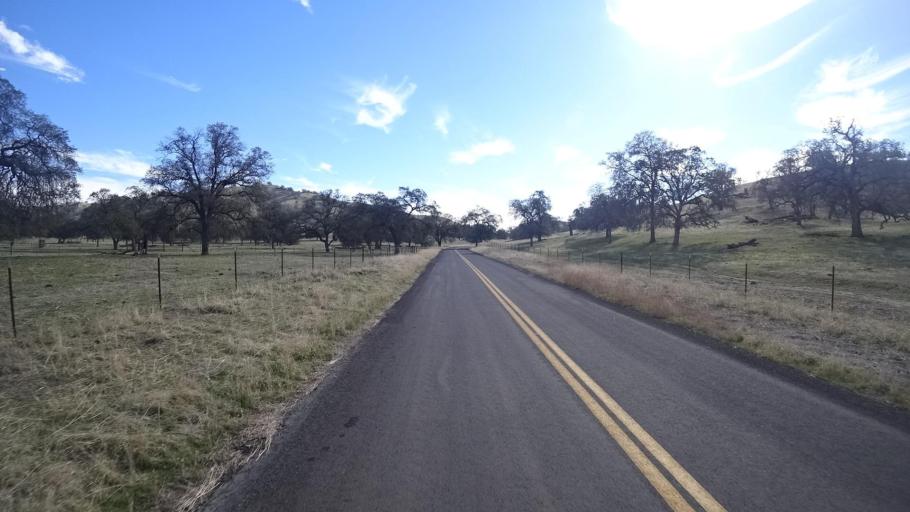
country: US
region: California
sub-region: Tulare County
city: Richgrove
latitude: 35.6679
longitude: -118.8488
